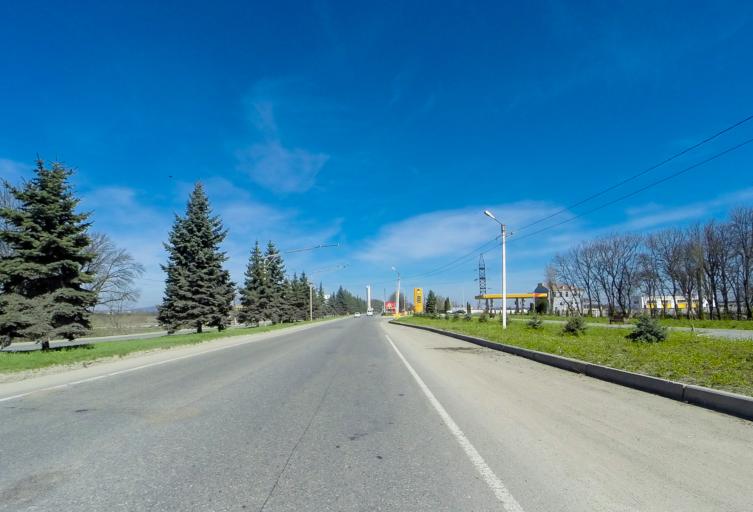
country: RU
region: Kabardino-Balkariya
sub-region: Gorod Nal'chik
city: Nal'chik
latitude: 43.5237
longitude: 43.6109
